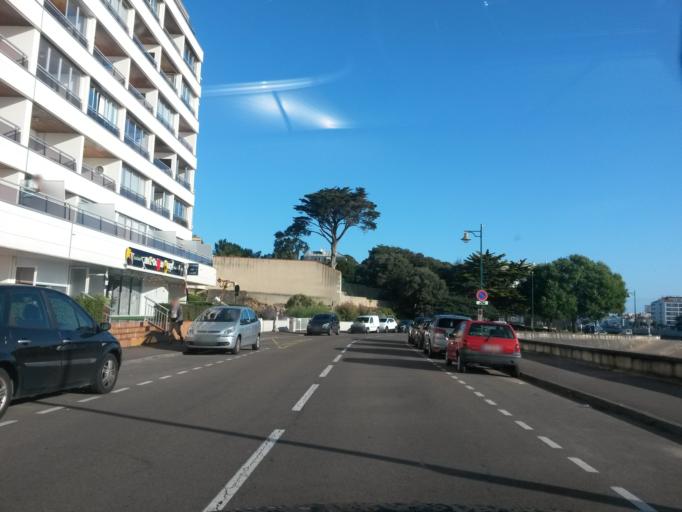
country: FR
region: Pays de la Loire
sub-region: Departement de la Vendee
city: Les Sables-d'Olonne
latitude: 46.4915
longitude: -1.7951
